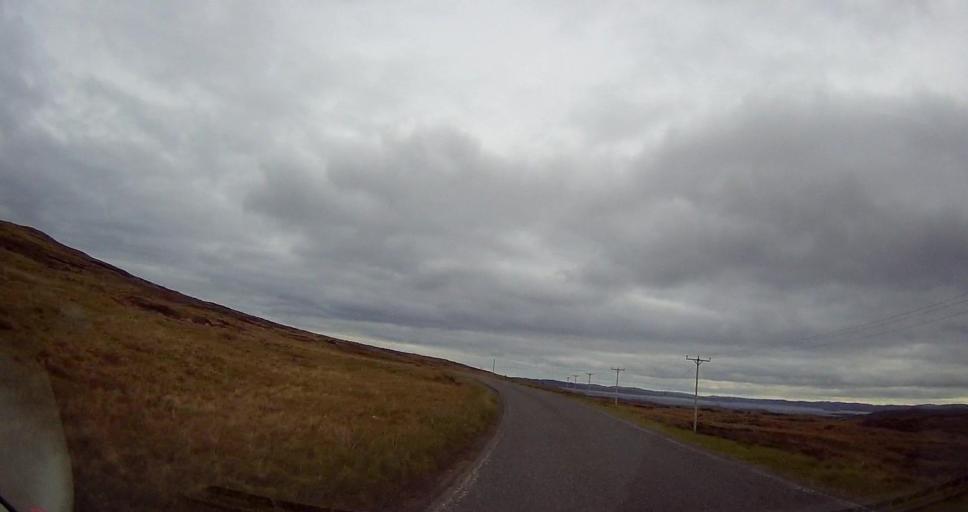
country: GB
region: Scotland
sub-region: Shetland Islands
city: Shetland
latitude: 60.5176
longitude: -1.0585
